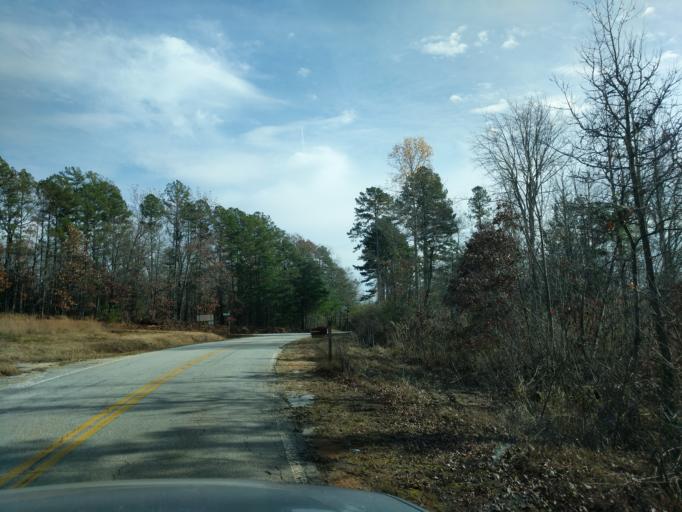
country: US
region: South Carolina
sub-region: Oconee County
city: Walhalla
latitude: 34.8326
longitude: -83.0512
